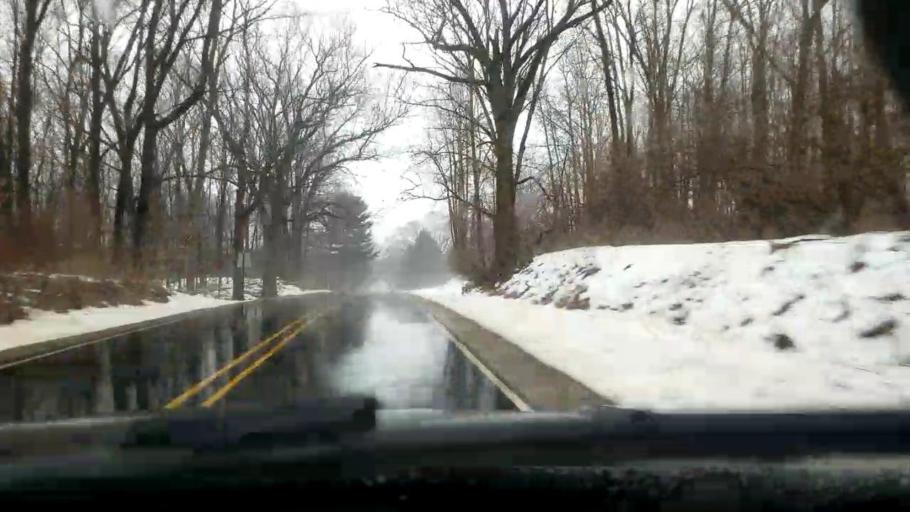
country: US
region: Michigan
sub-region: Jackson County
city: Grass Lake
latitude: 42.3211
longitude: -84.2617
